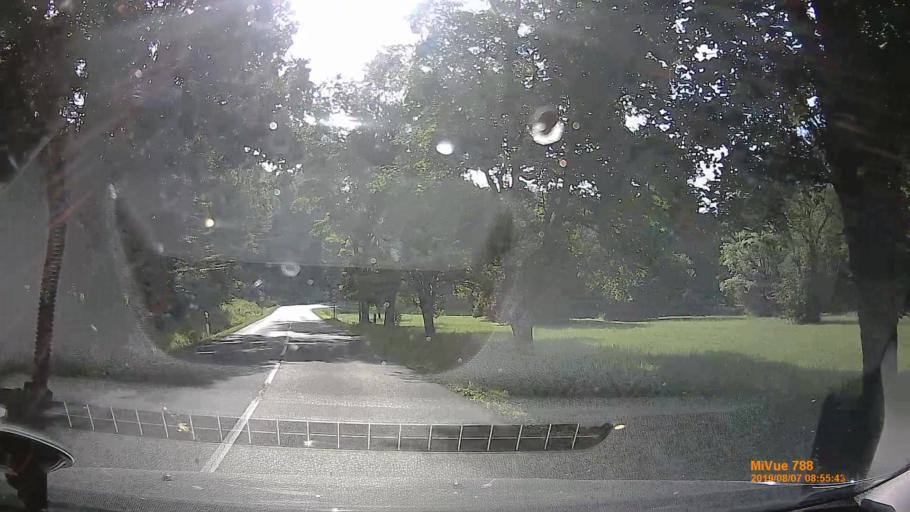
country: HU
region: Zala
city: Zalaegerszeg
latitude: 46.7341
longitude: 16.8828
